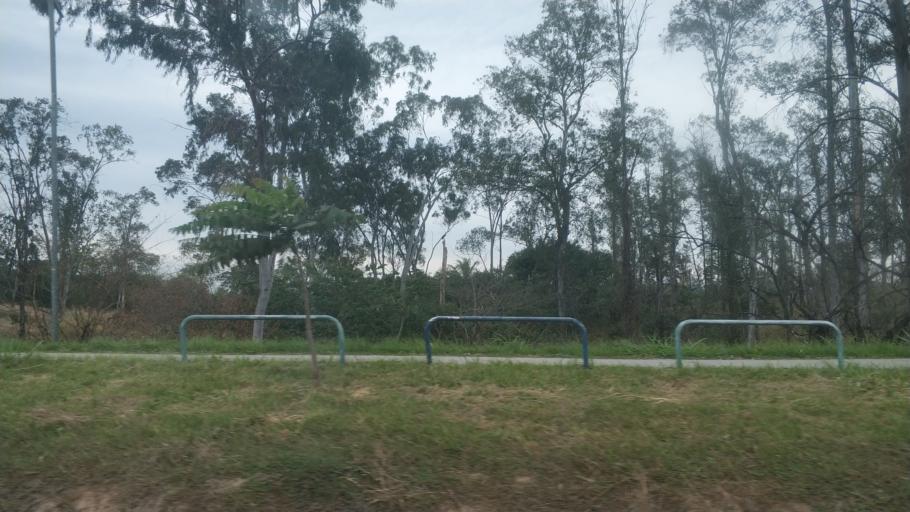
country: BR
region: Rio de Janeiro
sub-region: Seropedica
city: Seropedica
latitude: -22.7532
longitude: -43.6942
